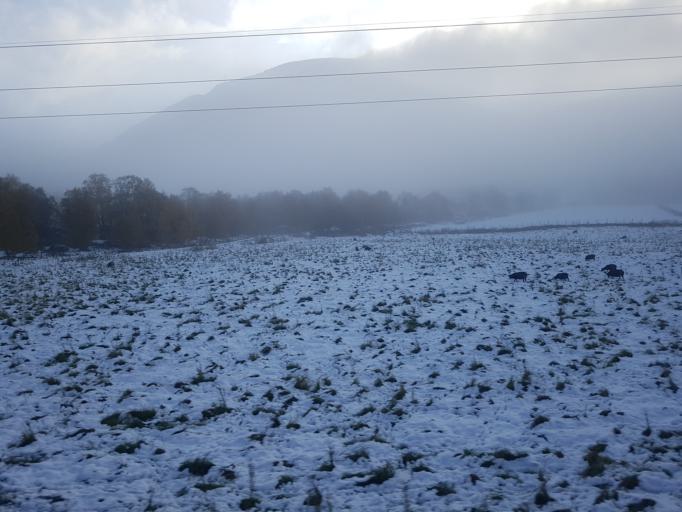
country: NO
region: Sor-Trondelag
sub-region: Oppdal
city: Oppdal
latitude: 62.5663
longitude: 9.6445
